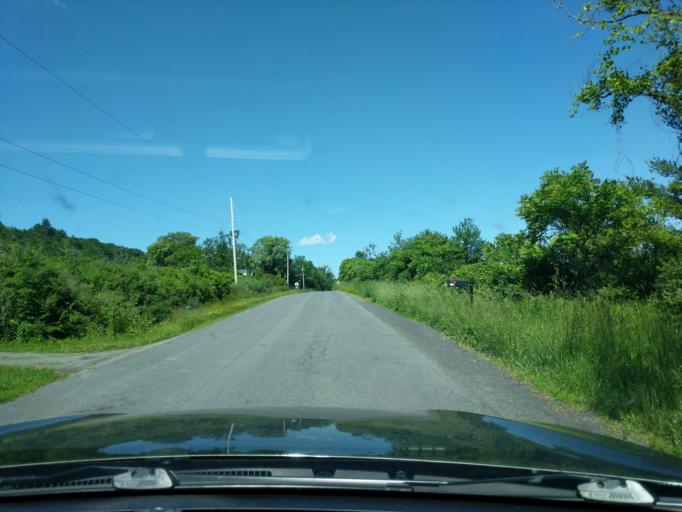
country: US
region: New York
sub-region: Tompkins County
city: Dryden
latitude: 42.3800
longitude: -76.3621
